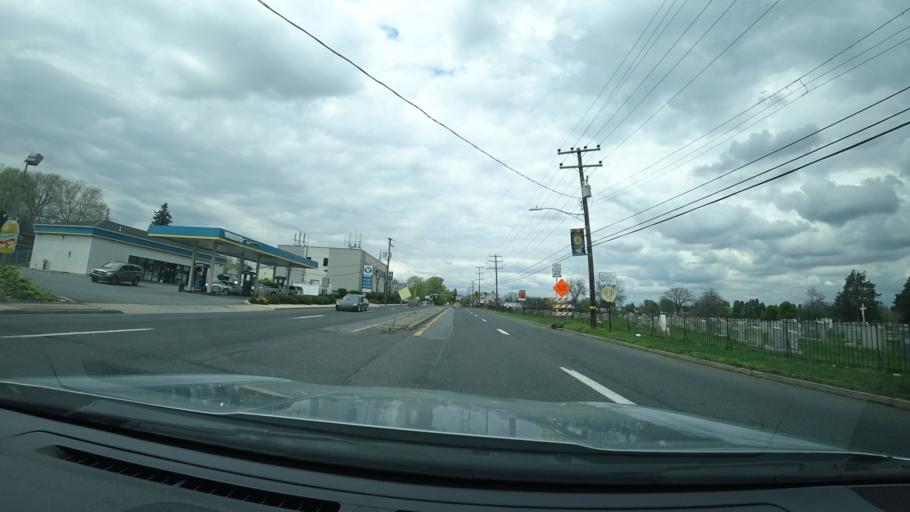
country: US
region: Pennsylvania
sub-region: Lehigh County
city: Fullerton
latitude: 40.6232
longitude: -75.4659
